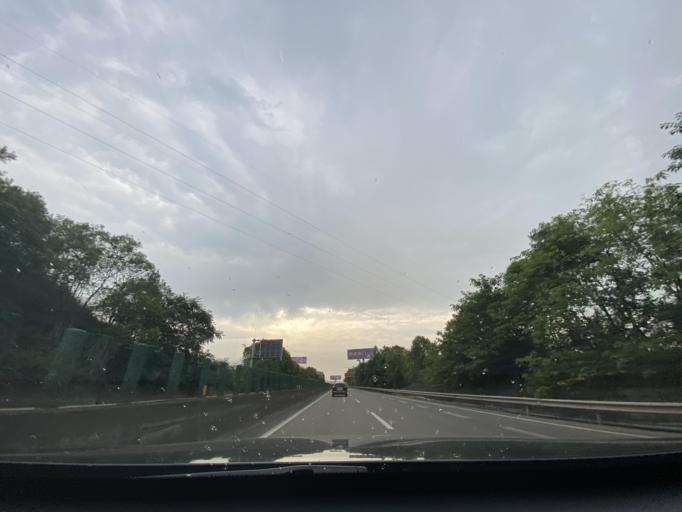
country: CN
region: Sichuan
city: Chonglong
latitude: 29.7597
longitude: 104.8302
